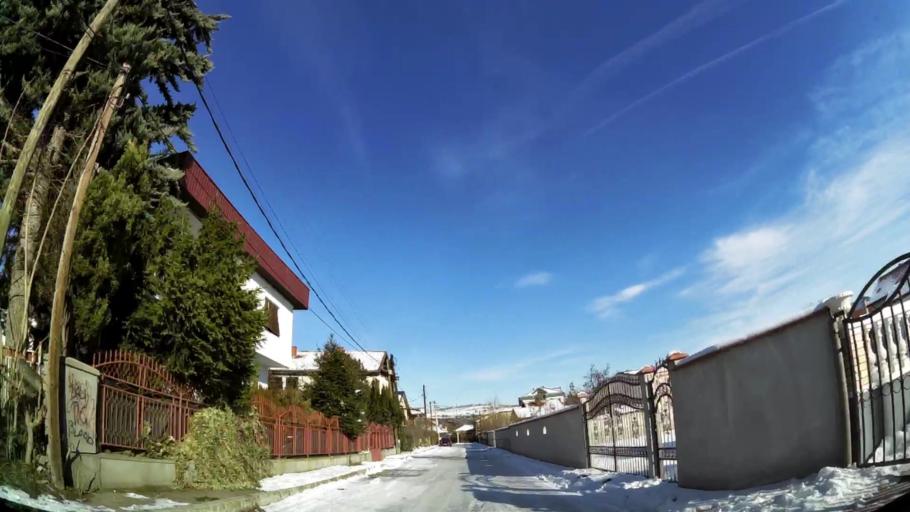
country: MK
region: Saraj
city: Saraj
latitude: 42.0055
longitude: 21.3399
